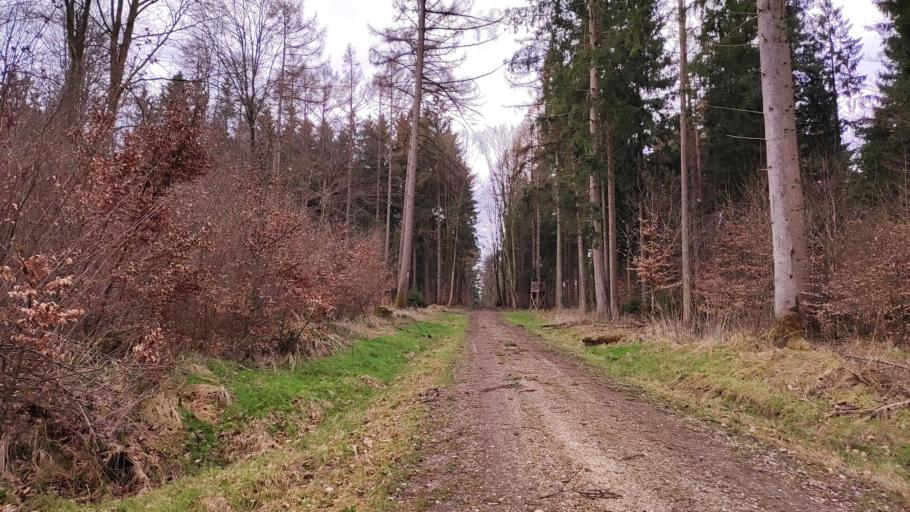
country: DE
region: Bavaria
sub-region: Swabia
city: Landensberg
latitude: 48.4313
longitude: 10.5567
